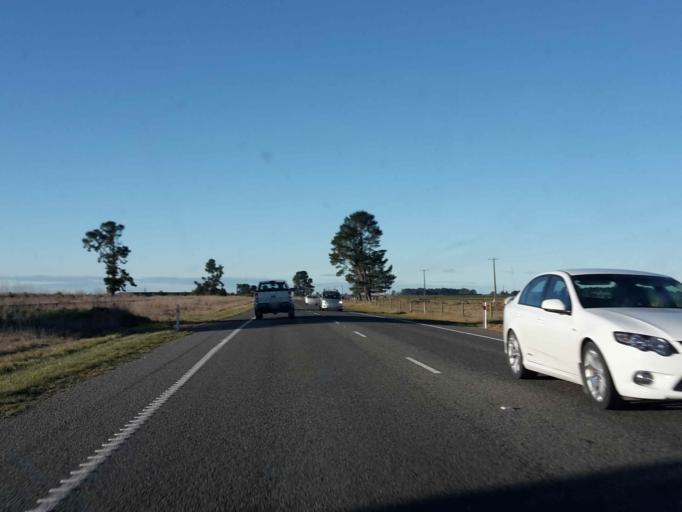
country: NZ
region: Canterbury
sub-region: Ashburton District
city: Tinwald
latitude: -44.0258
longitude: 171.4944
